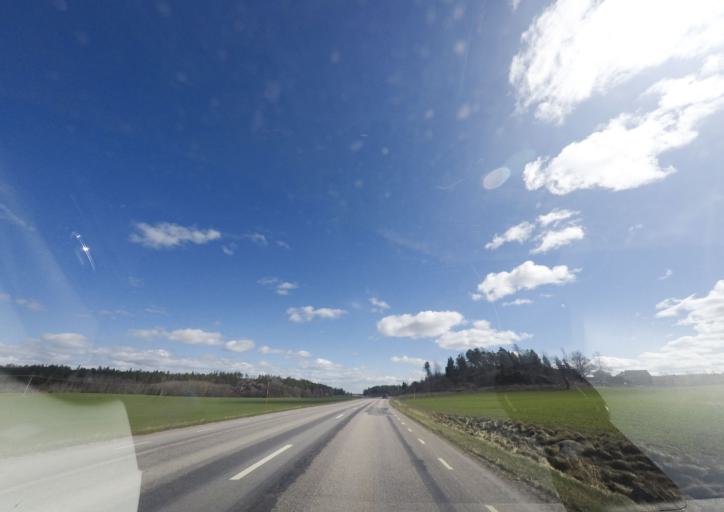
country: SE
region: Soedermanland
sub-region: Nykopings Kommun
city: Olstorp
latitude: 58.7466
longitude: 16.6426
